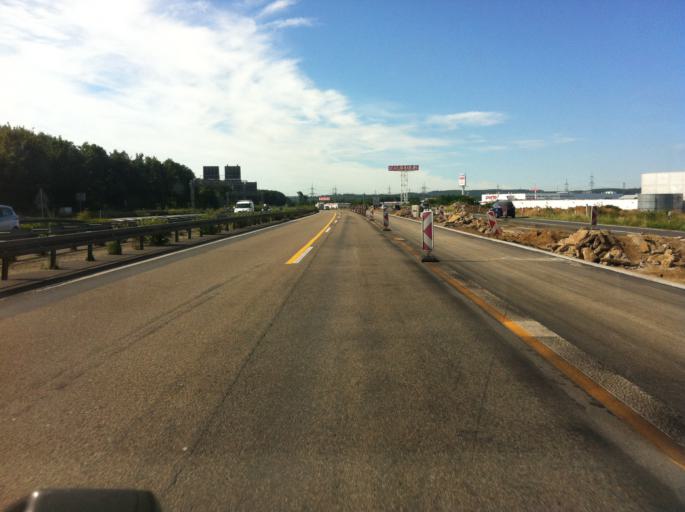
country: DE
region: North Rhine-Westphalia
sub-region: Regierungsbezirk Koln
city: Frechen
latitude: 50.9247
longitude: 6.8443
